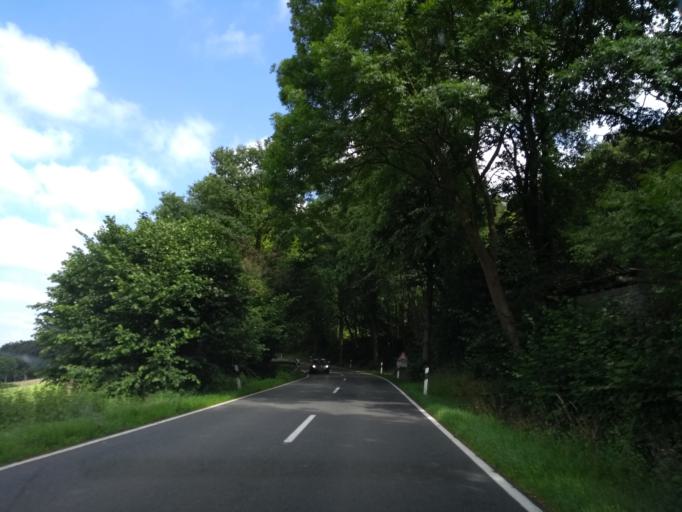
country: DE
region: Lower Saxony
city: Bad Pyrmont
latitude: 51.9760
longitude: 9.2885
